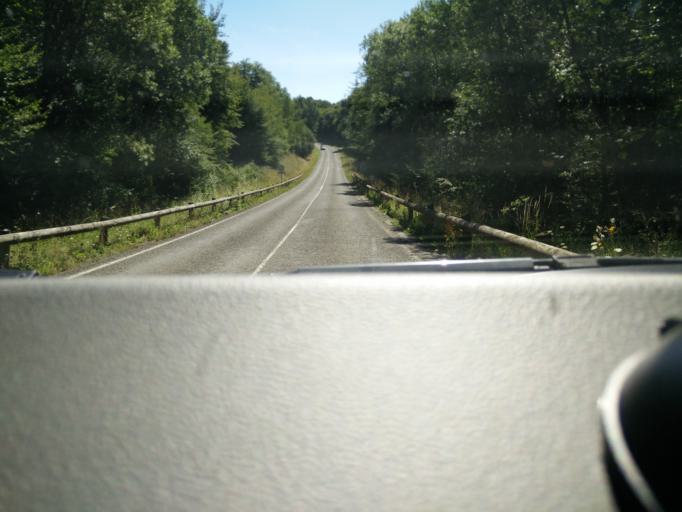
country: FR
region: Nord-Pas-de-Calais
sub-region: Departement du Nord
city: Trelon
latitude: 50.1228
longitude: 4.1356
